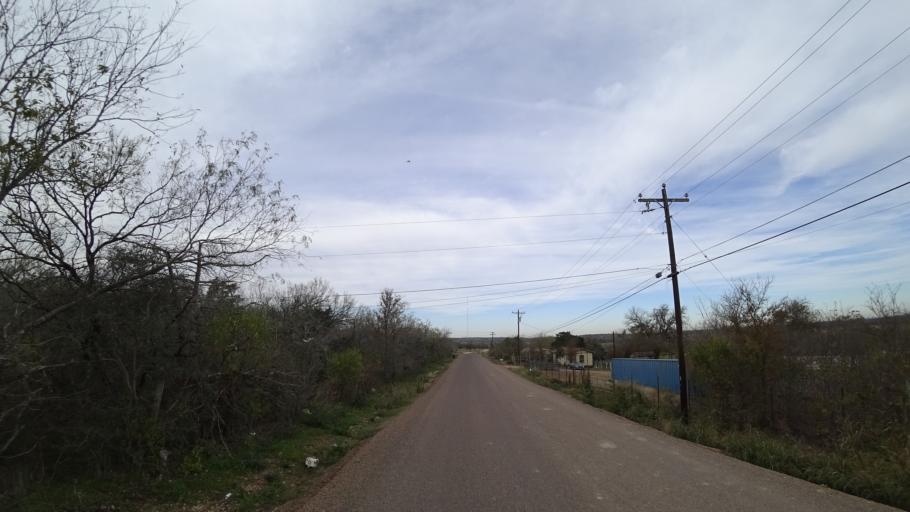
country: US
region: Texas
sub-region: Travis County
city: Garfield
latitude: 30.1144
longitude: -97.5717
